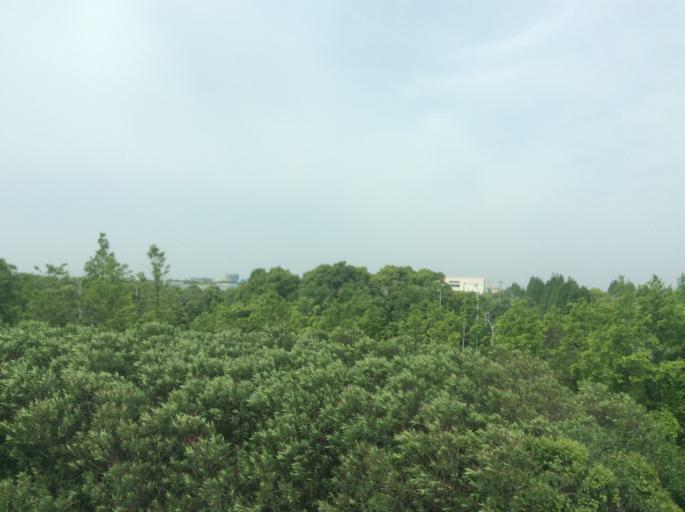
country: CN
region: Shanghai Shi
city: Laogang
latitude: 31.1775
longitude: 121.7869
